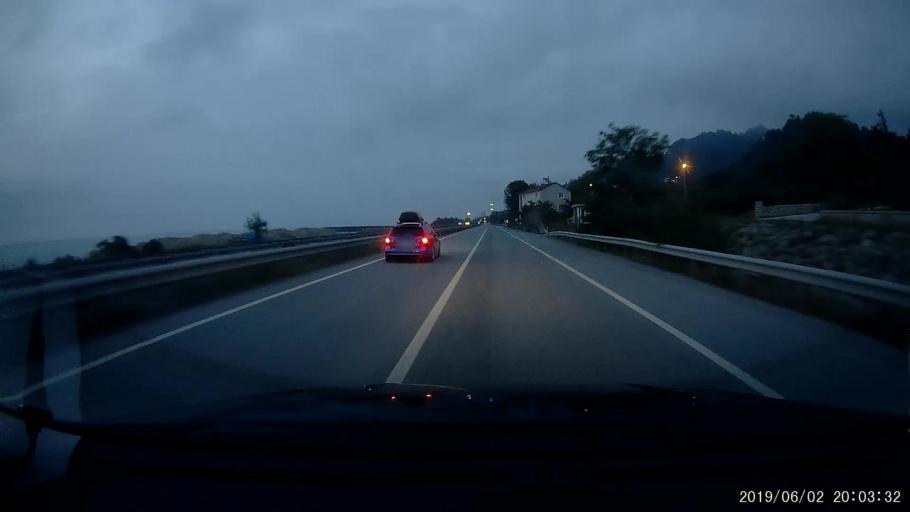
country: TR
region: Giresun
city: Tirebolu
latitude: 41.0221
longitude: 38.8946
